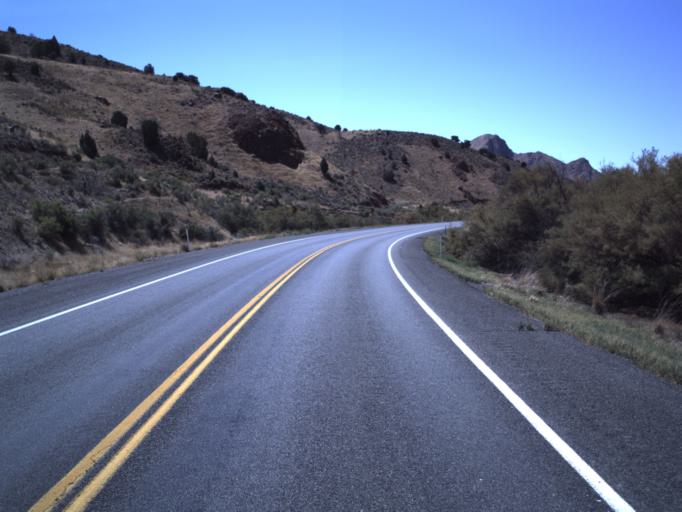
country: US
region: Utah
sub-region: Juab County
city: Nephi
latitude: 39.5816
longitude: -112.1716
